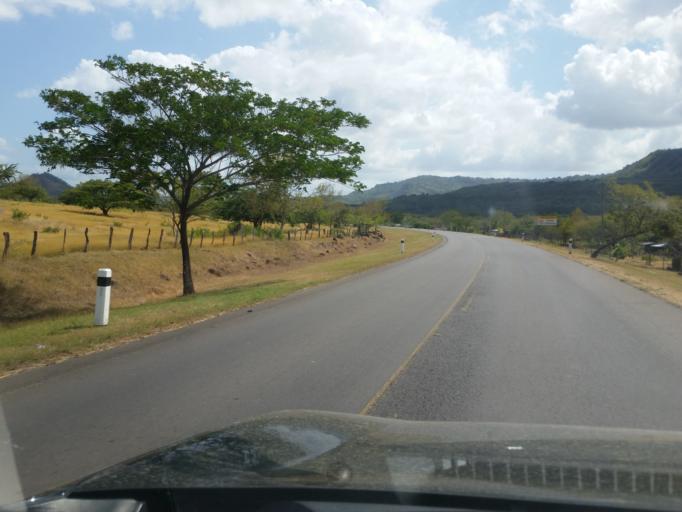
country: NI
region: Chontales
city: Comalapa
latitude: 12.1976
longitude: -85.6234
